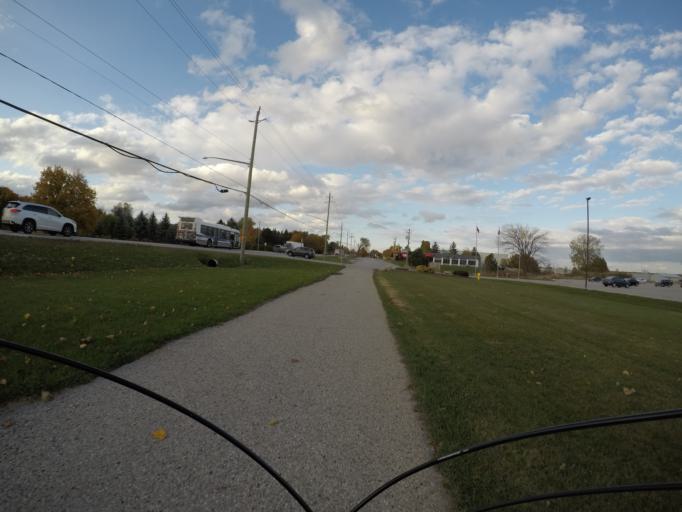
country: CA
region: Ontario
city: Waterloo
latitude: 43.5853
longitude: -80.5617
